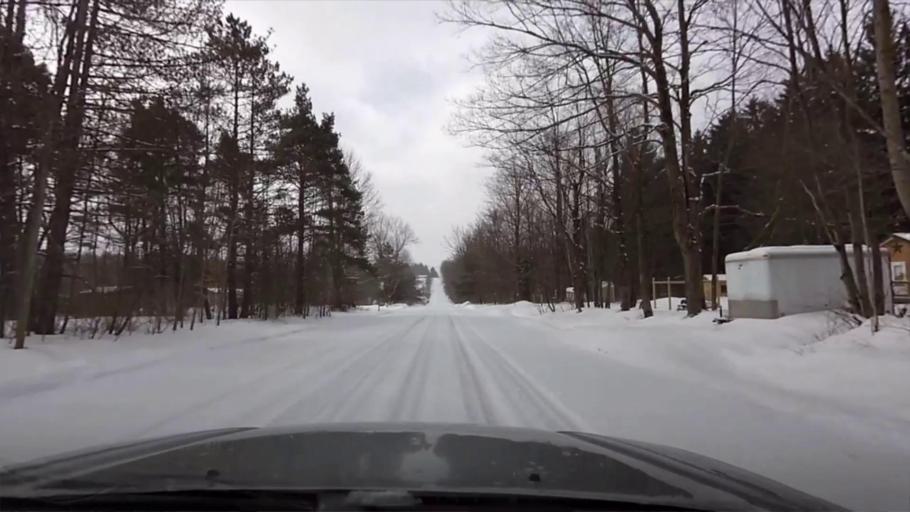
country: US
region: New York
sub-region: Cattaraugus County
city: Franklinville
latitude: 42.3241
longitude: -78.3540
